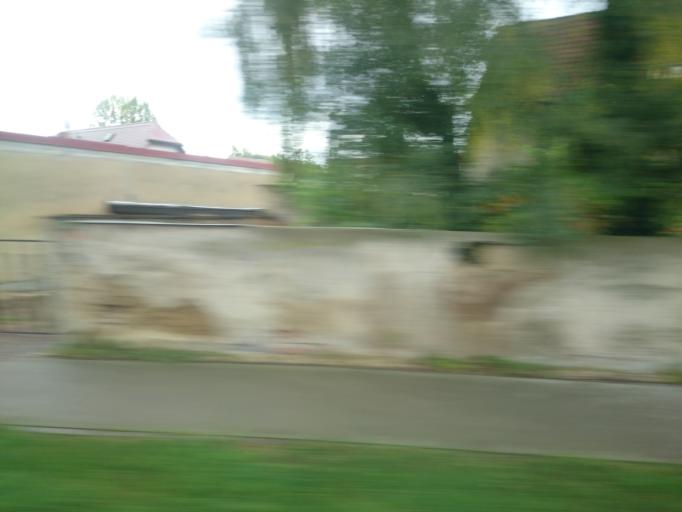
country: DE
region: Saxony-Anhalt
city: Halle (Saale)
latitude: 51.4933
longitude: 12.0032
